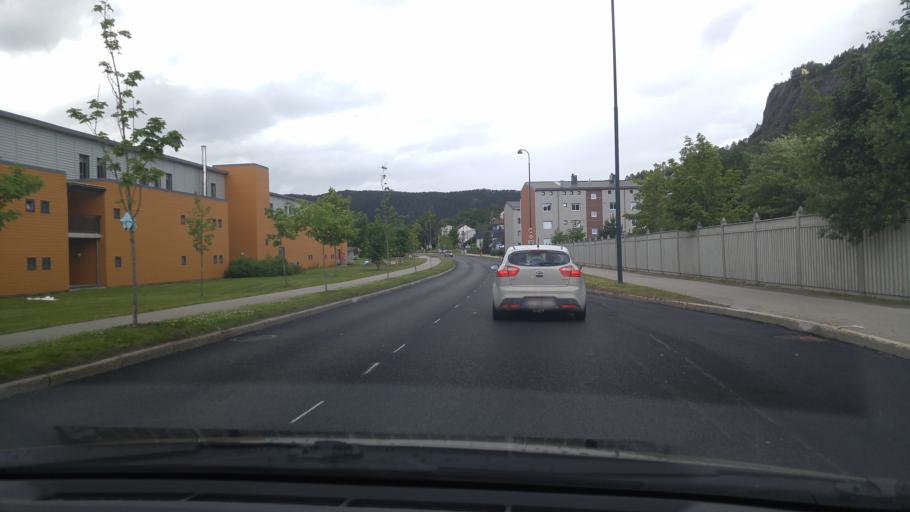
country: NO
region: Nord-Trondelag
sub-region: Namsos
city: Namsos
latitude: 64.4689
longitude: 11.5064
